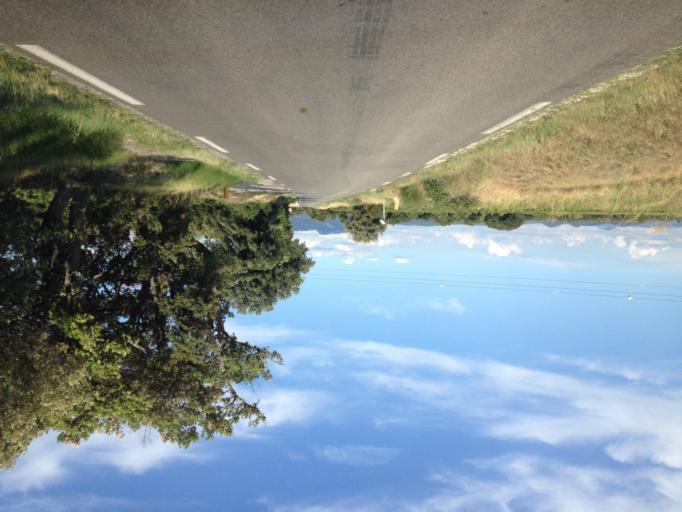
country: FR
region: Provence-Alpes-Cote d'Azur
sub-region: Departement du Vaucluse
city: Camaret-sur-Aigues
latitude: 44.1642
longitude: 4.8975
